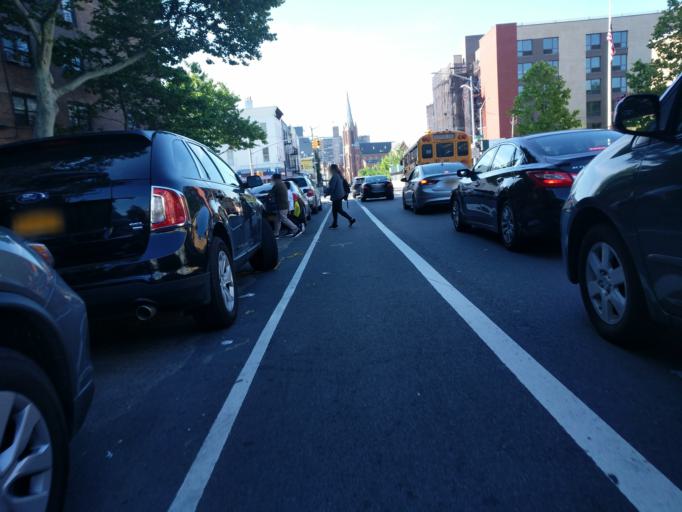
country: US
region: New York
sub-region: Queens County
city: Long Island City
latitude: 40.6978
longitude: -73.9439
